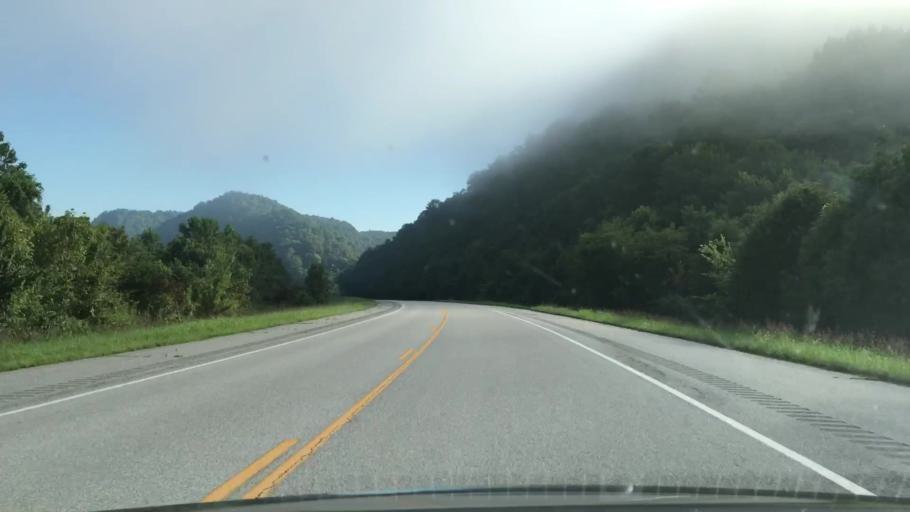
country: US
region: Tennessee
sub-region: Jackson County
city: Gainesboro
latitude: 36.4438
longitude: -85.5823
